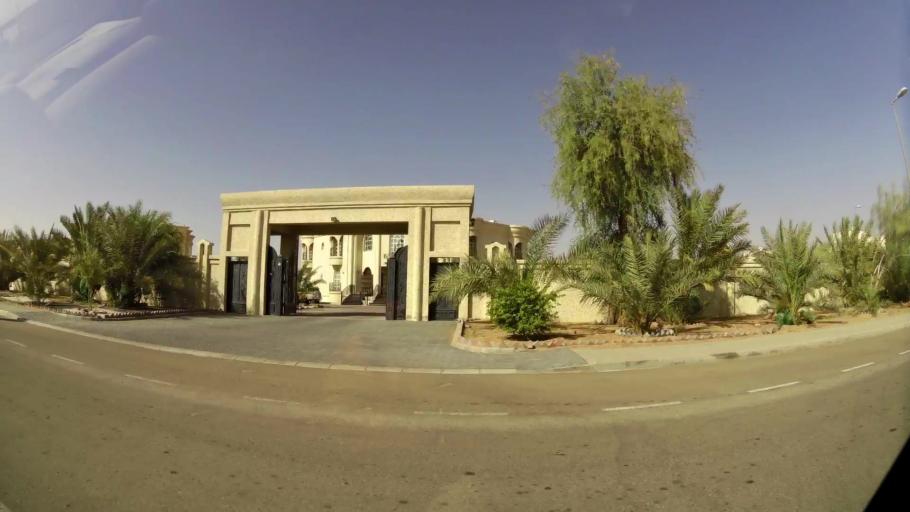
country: OM
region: Al Buraimi
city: Al Buraymi
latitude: 24.3502
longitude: 55.7874
